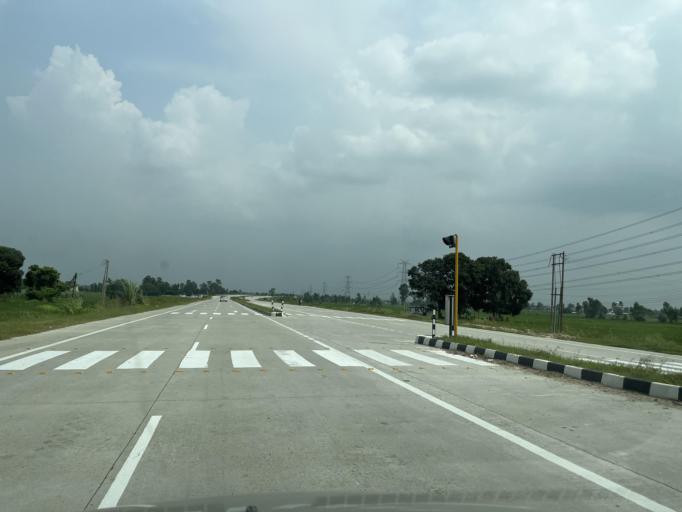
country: IN
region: Uttarakhand
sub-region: Udham Singh Nagar
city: Jaspur
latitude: 29.2917
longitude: 78.8486
